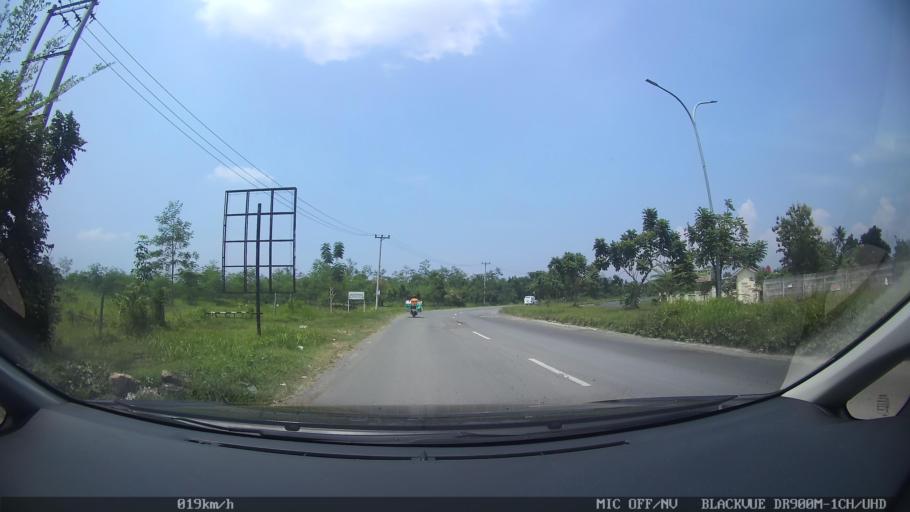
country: ID
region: Lampung
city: Kedaton
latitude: -5.3543
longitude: 105.3206
